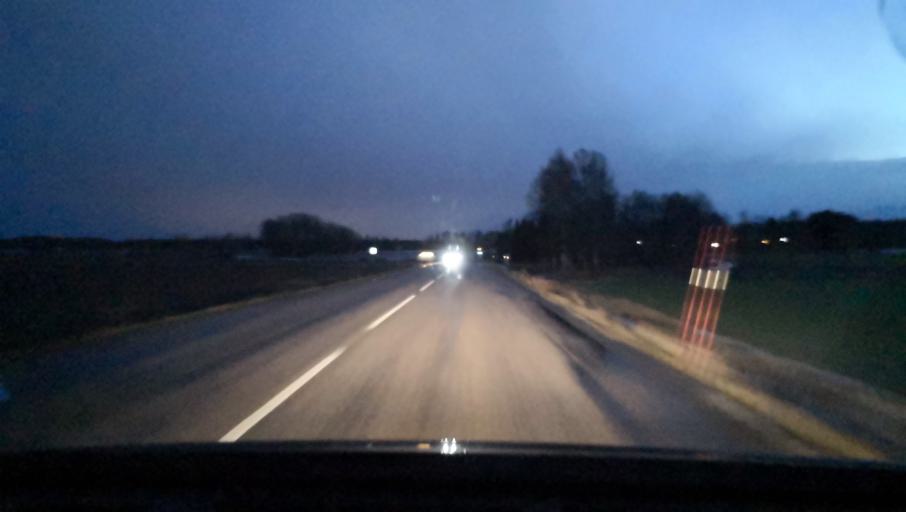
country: SE
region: Vaestmanland
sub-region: Vasteras
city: Skultuna
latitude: 59.7690
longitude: 16.4613
